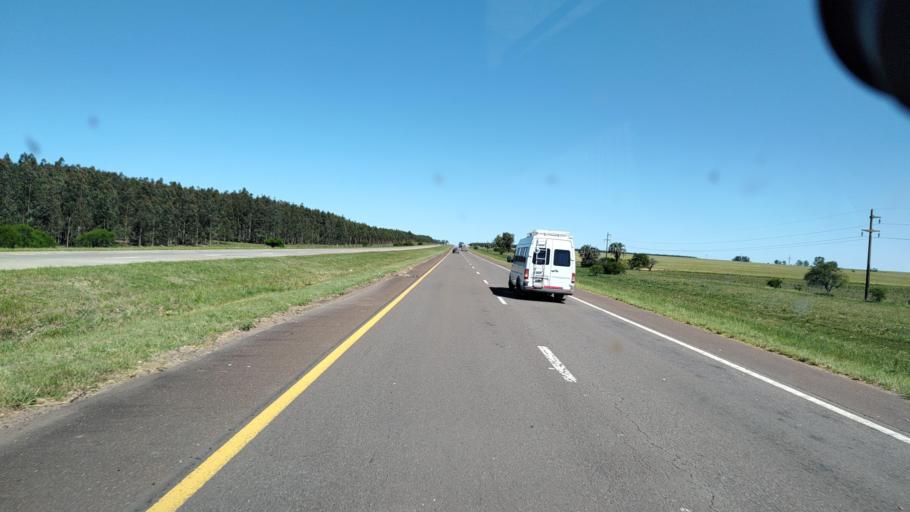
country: AR
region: Entre Rios
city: Villa Elisa
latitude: -32.0147
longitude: -58.2870
